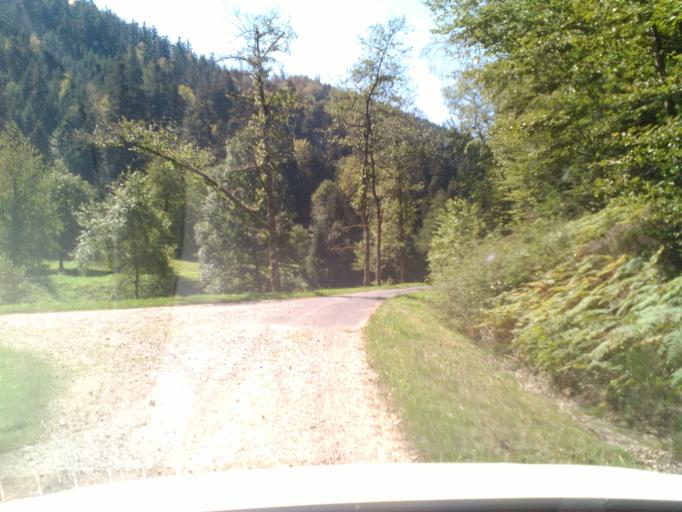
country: FR
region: Lorraine
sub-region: Departement des Vosges
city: Senones
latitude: 48.4237
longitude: 6.9506
